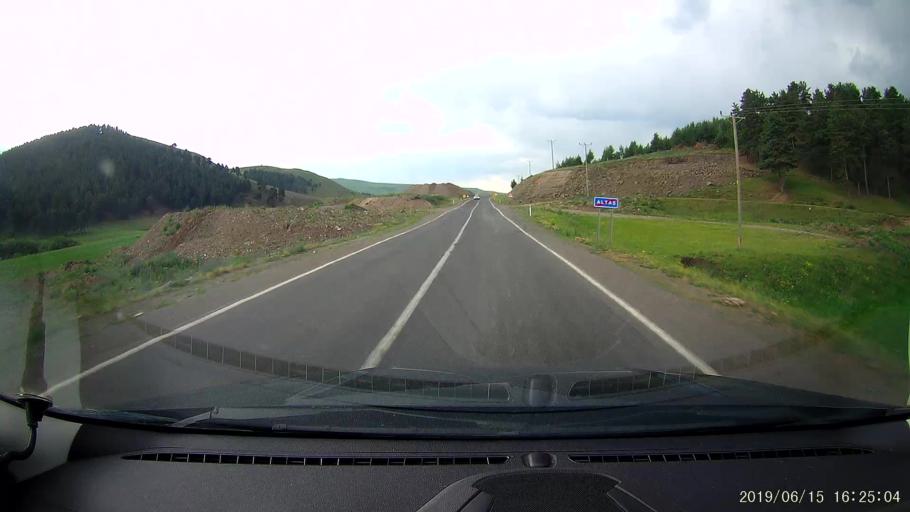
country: TR
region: Ardahan
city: Hanak
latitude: 41.1586
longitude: 42.8716
